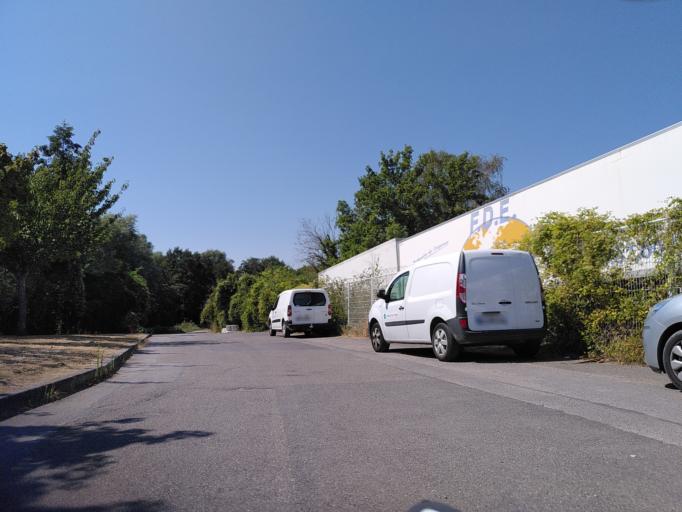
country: FR
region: Ile-de-France
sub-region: Departement de l'Essonne
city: Ollainville
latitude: 48.5888
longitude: 2.2302
